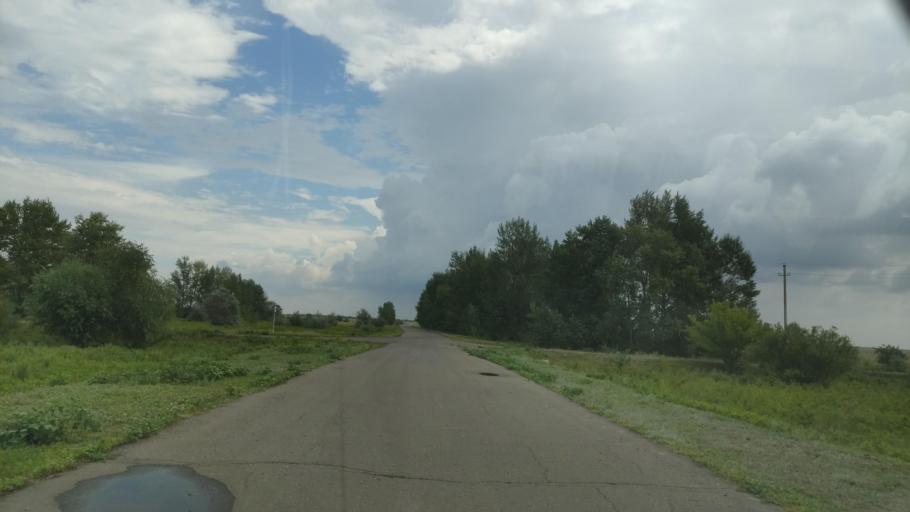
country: KZ
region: Pavlodar
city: Pavlodar
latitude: 52.6351
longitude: 77.3300
